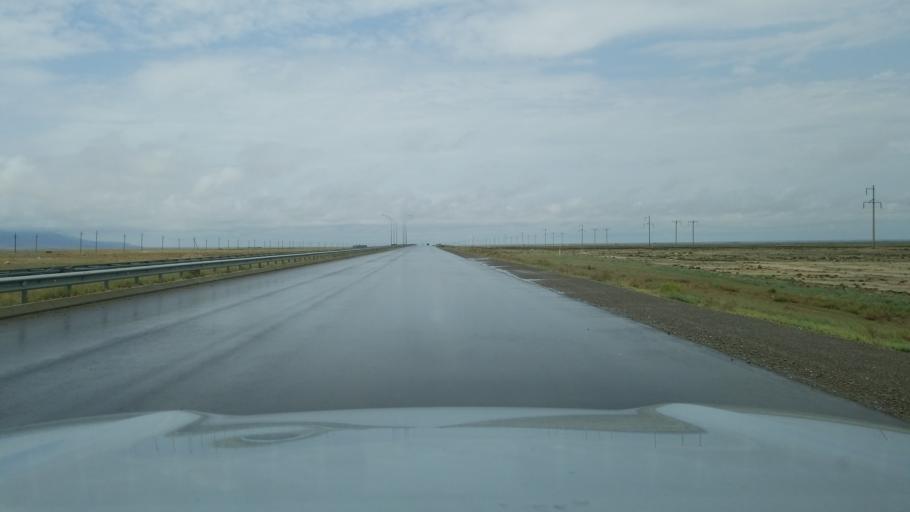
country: TM
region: Balkan
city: Gazanjyk
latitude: 39.1645
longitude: 55.8319
